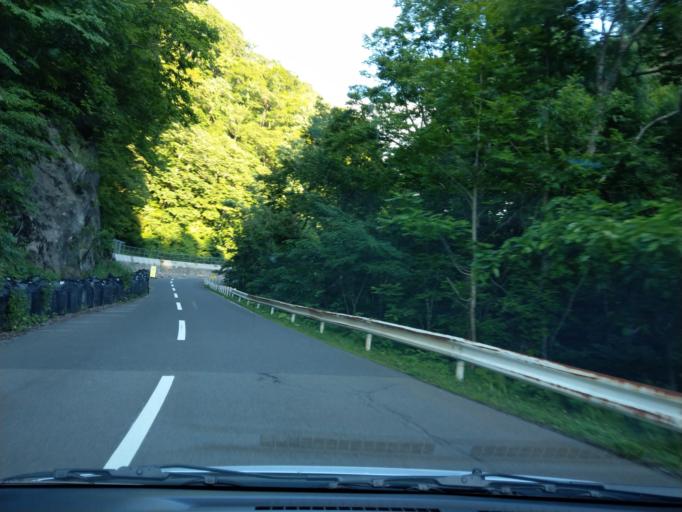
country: JP
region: Akita
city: Kakunodatemachi
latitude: 39.8763
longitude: 140.4788
